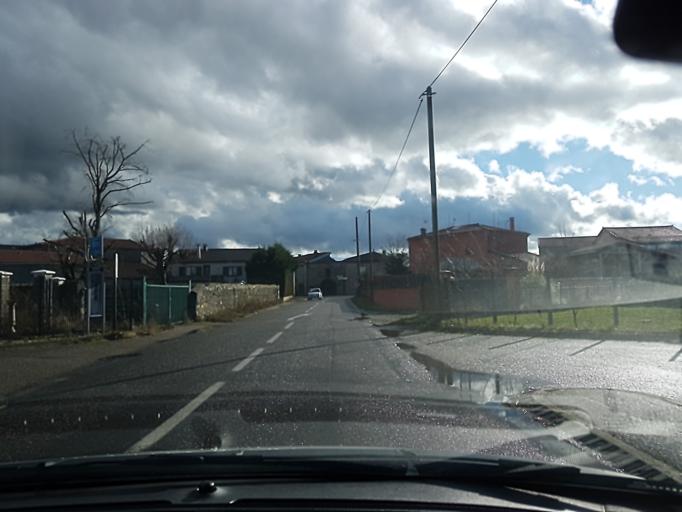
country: FR
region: Rhone-Alpes
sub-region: Departement du Rhone
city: Saint-Andeol-le-Chateau
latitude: 45.5897
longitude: 4.6653
